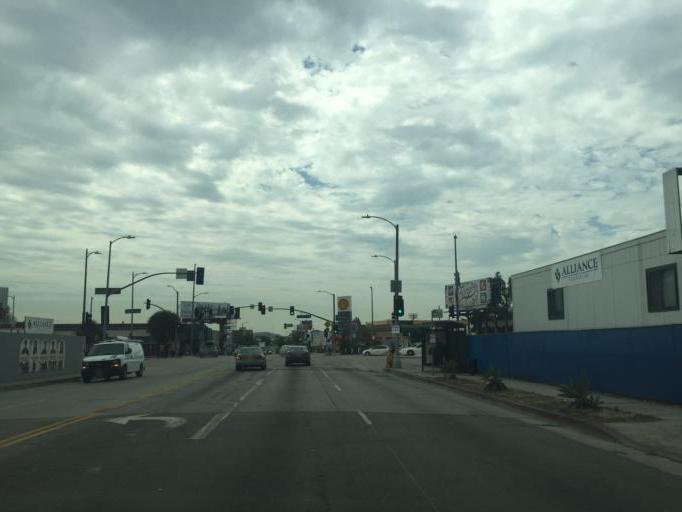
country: US
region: California
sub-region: Los Angeles County
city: West Hollywood
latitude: 34.0592
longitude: -118.3634
